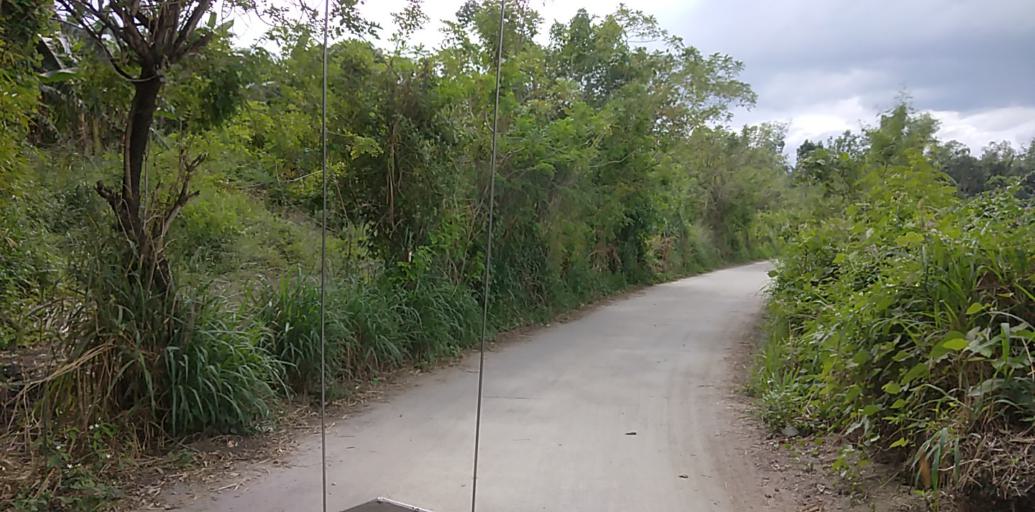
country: PH
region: Central Luzon
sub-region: Province of Pampanga
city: Porac
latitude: 15.0588
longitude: 120.5333
